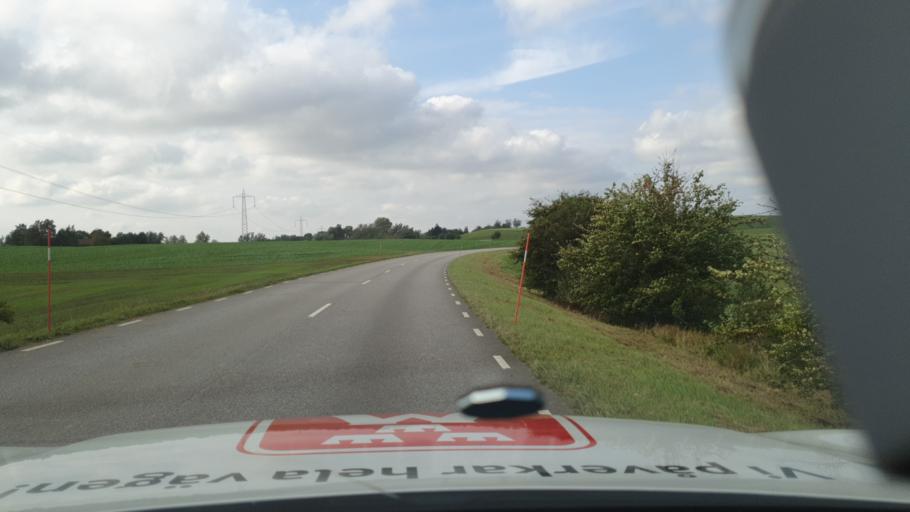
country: SE
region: Skane
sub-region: Malmo
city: Oxie
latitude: 55.4926
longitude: 13.1394
